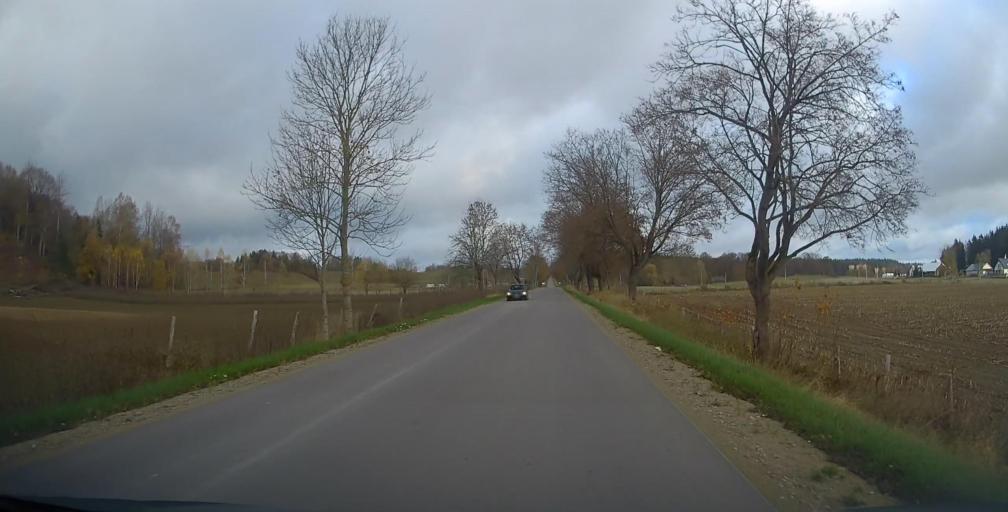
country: PL
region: Podlasie
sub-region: Suwalki
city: Suwalki
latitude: 54.3002
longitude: 22.8787
